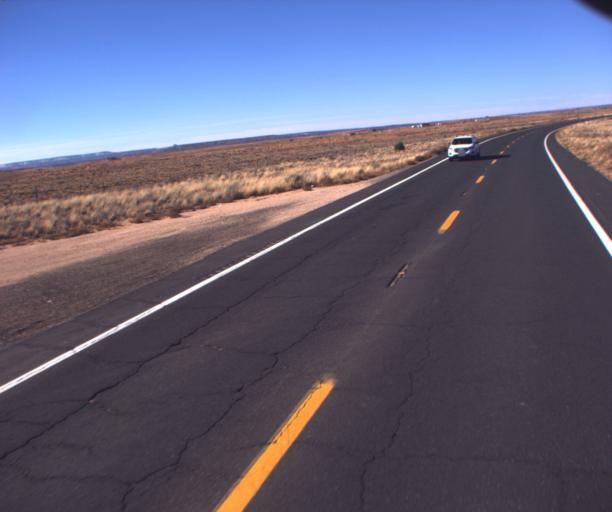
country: US
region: Arizona
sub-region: Coconino County
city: Kaibito
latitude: 36.4827
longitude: -110.7042
